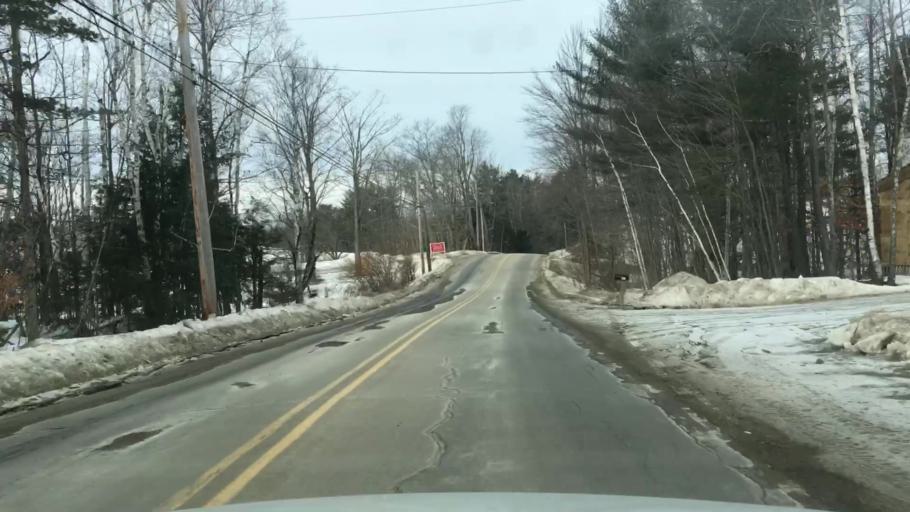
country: US
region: Maine
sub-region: Kennebec County
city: Chelsea
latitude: 44.2573
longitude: -69.6433
